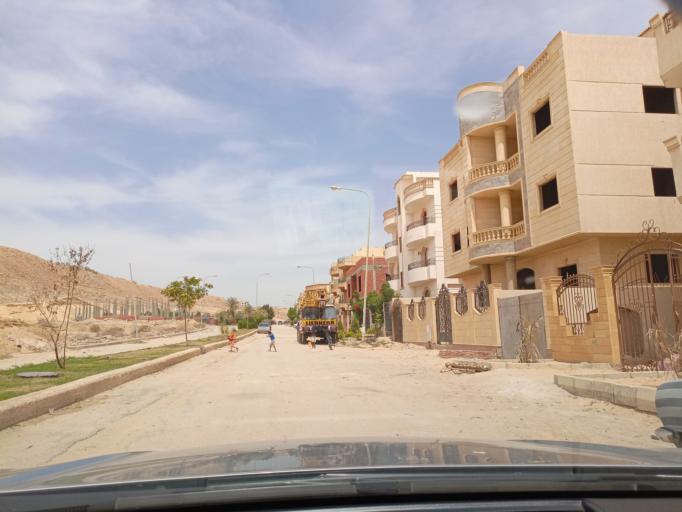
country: EG
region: Muhafazat al Qalyubiyah
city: Al Khankah
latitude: 30.2377
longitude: 31.4861
